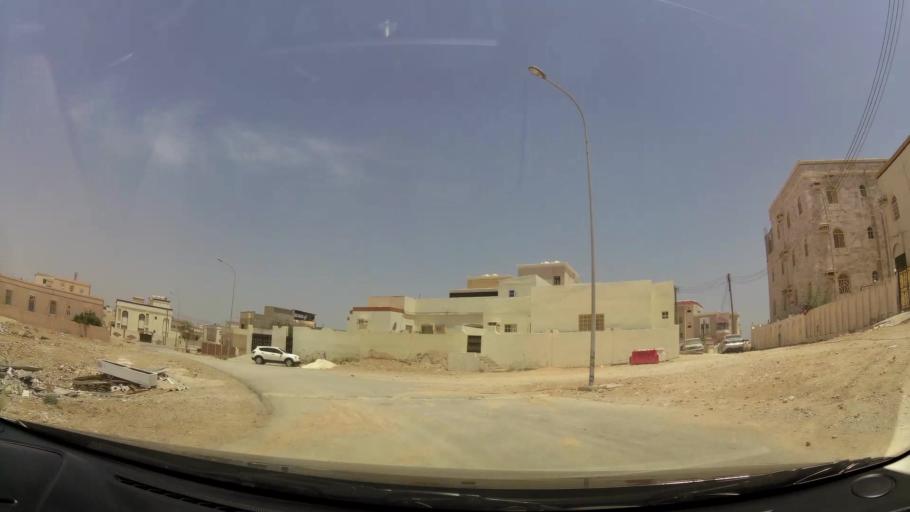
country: OM
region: Zufar
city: Salalah
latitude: 17.0789
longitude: 54.1494
